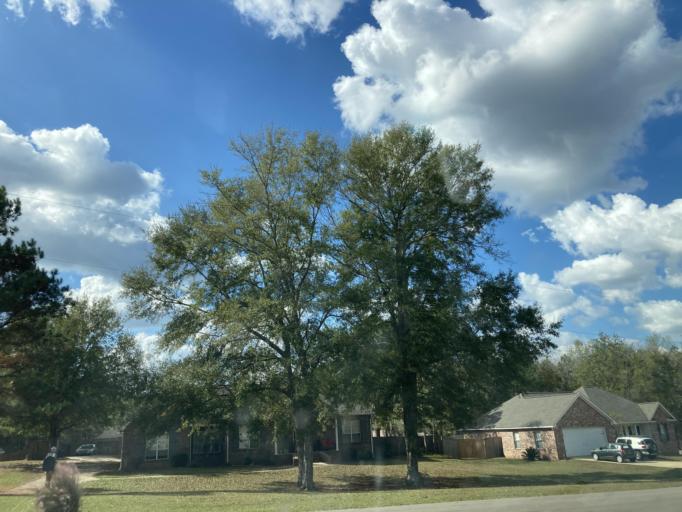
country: US
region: Mississippi
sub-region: Lamar County
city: Sumrall
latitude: 31.3984
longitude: -89.5362
